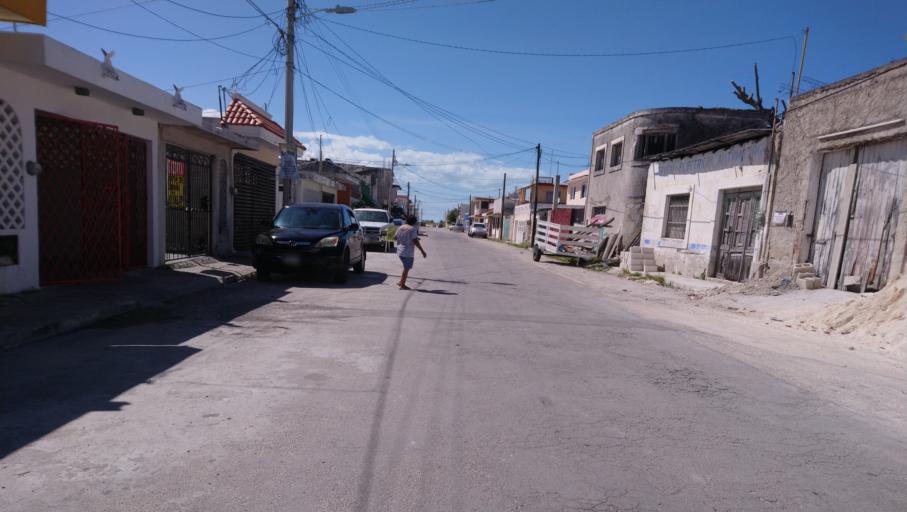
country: MX
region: Yucatan
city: Progreso de Castro
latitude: 21.2843
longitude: -89.6683
